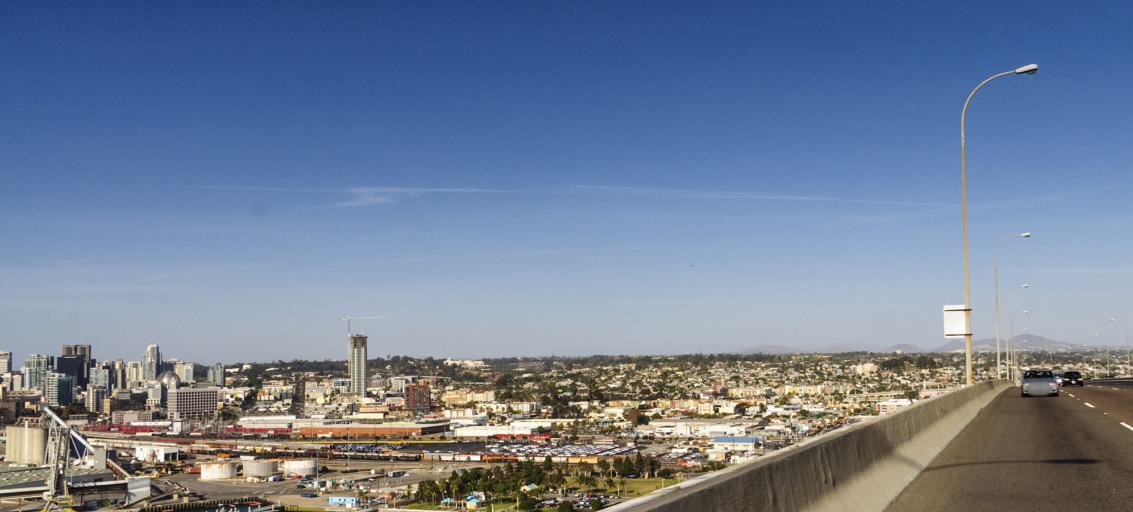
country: US
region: California
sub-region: San Diego County
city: San Diego
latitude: 32.6917
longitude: -117.1515
